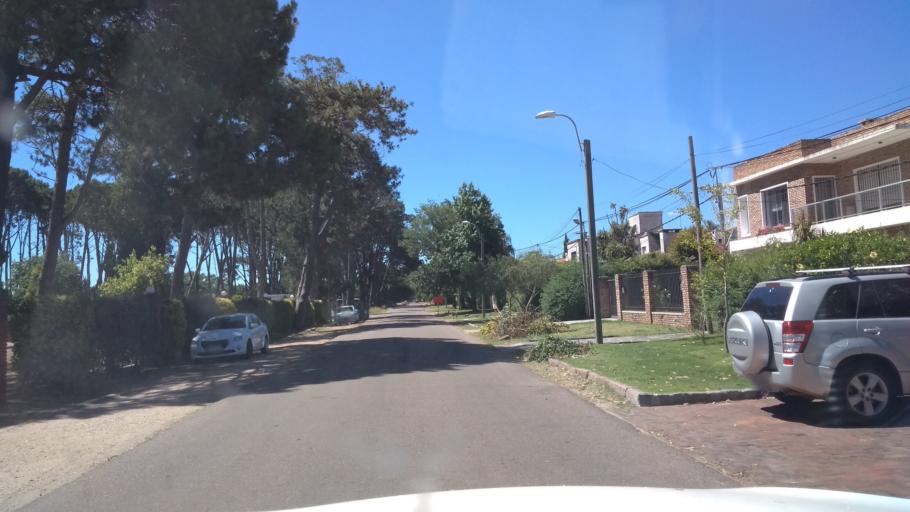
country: UY
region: Canelones
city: Paso de Carrasco
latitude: -34.8751
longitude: -56.0609
